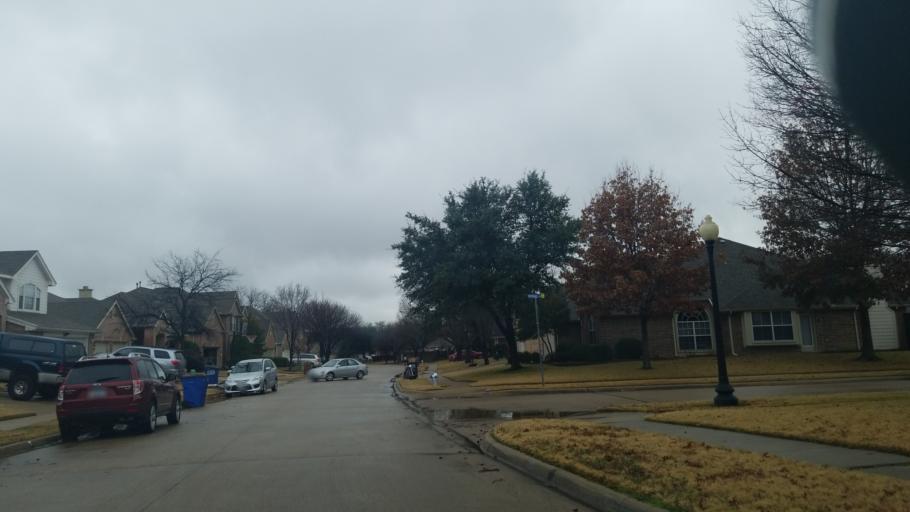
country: US
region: Texas
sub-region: Denton County
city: Corinth
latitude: 33.1525
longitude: -97.0842
